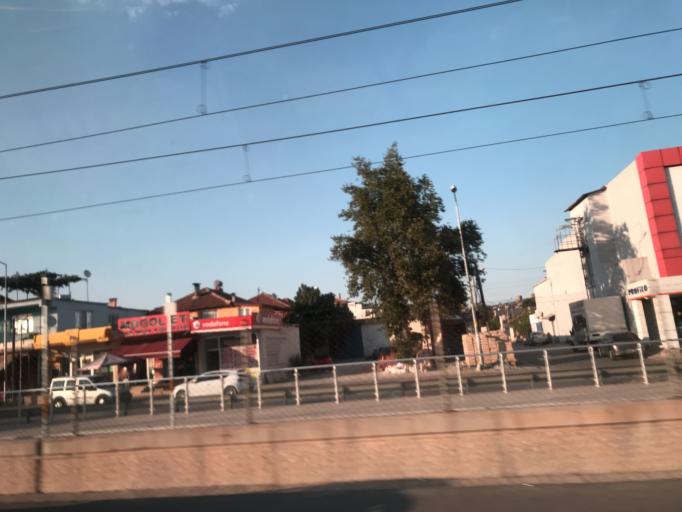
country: TR
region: Antalya
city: Antalya
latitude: 36.9379
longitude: 30.6529
